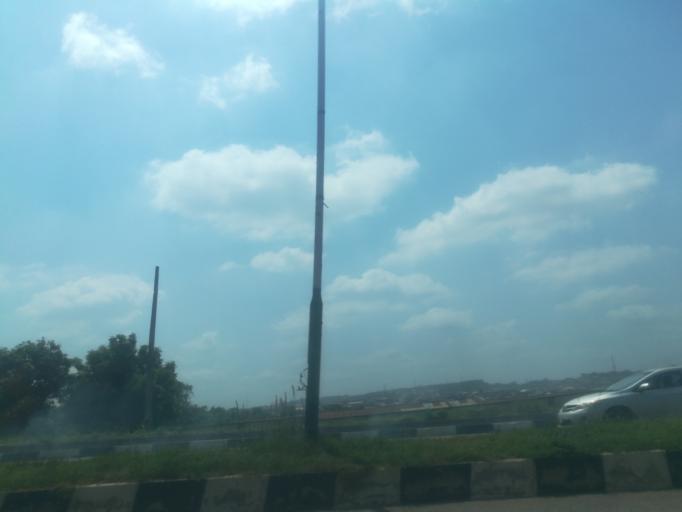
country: NG
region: Ogun
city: Abeokuta
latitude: 7.1460
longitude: 3.3656
